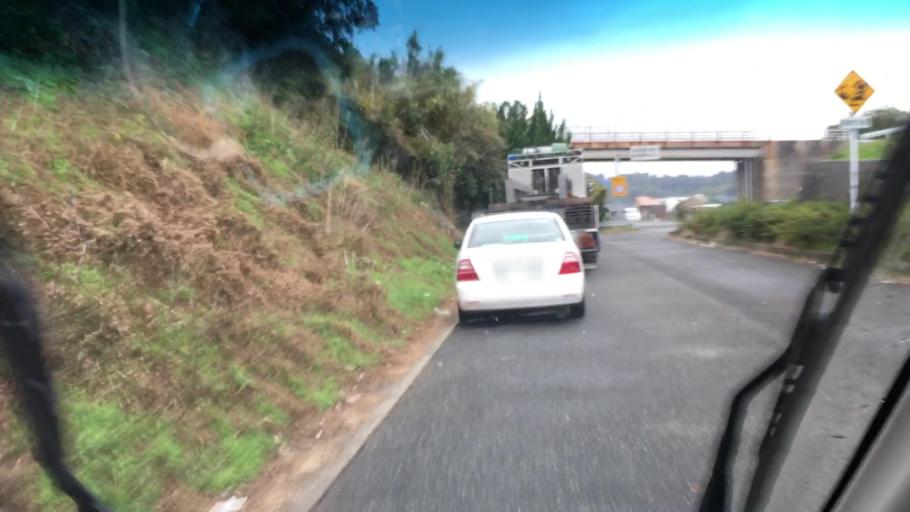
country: JP
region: Saga Prefecture
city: Karatsu
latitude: 33.5006
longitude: 130.0854
